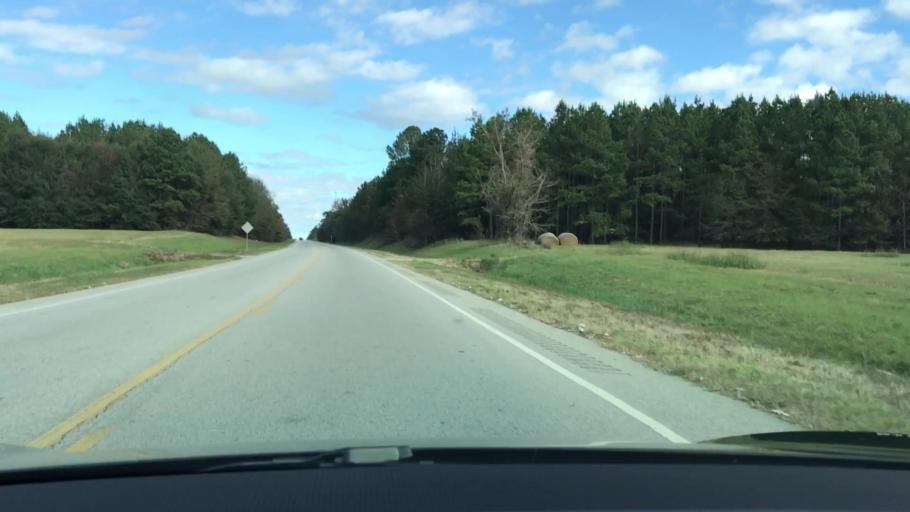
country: US
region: Georgia
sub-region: Jefferson County
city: Wadley
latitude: 32.8966
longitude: -82.4006
